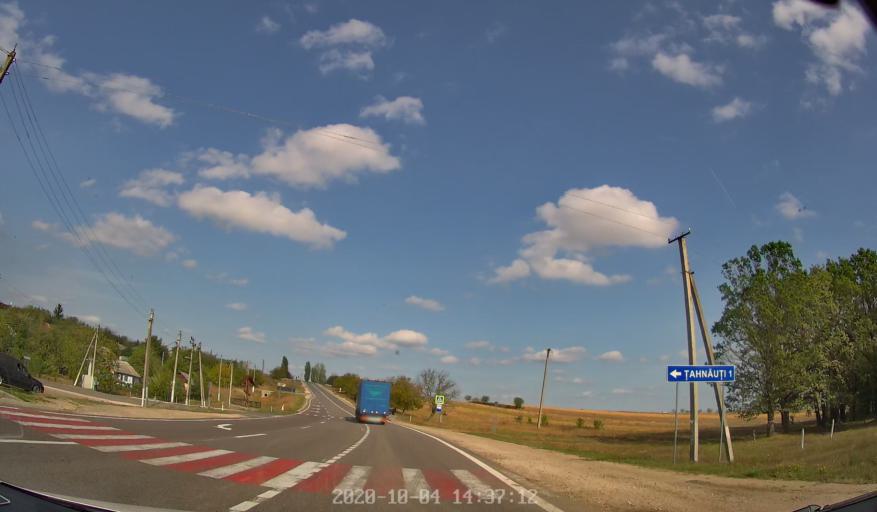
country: MD
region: Rezina
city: Rezina
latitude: 47.7324
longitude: 28.8752
